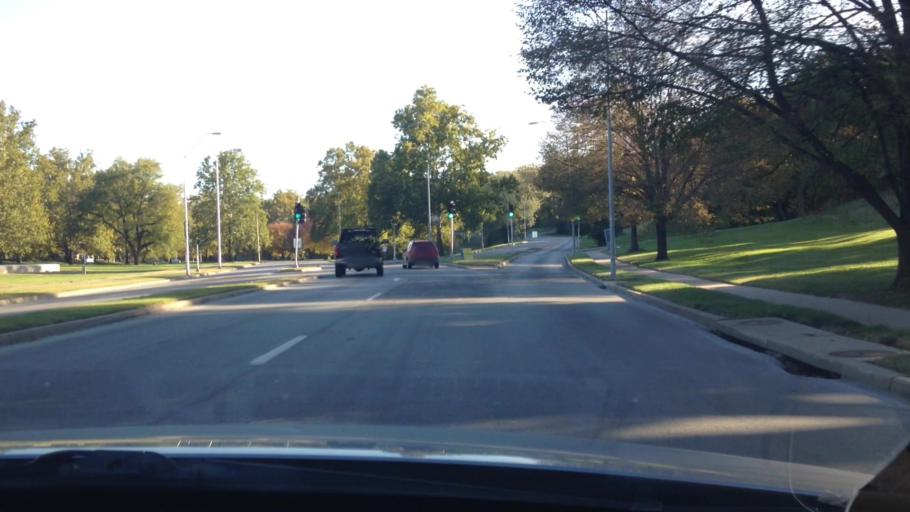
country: US
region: Kansas
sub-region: Johnson County
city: Westwood
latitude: 39.0518
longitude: -94.5794
